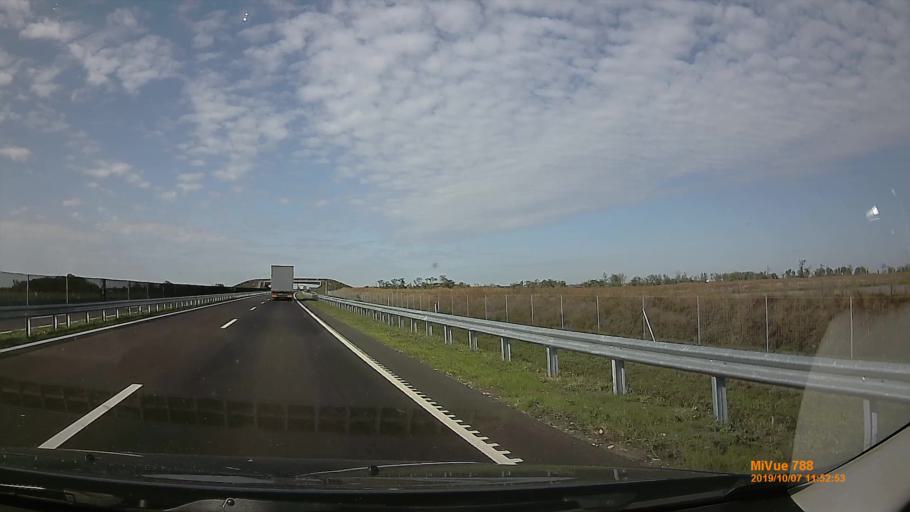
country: HU
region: Bekes
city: Szarvas
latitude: 46.8161
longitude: 20.6196
